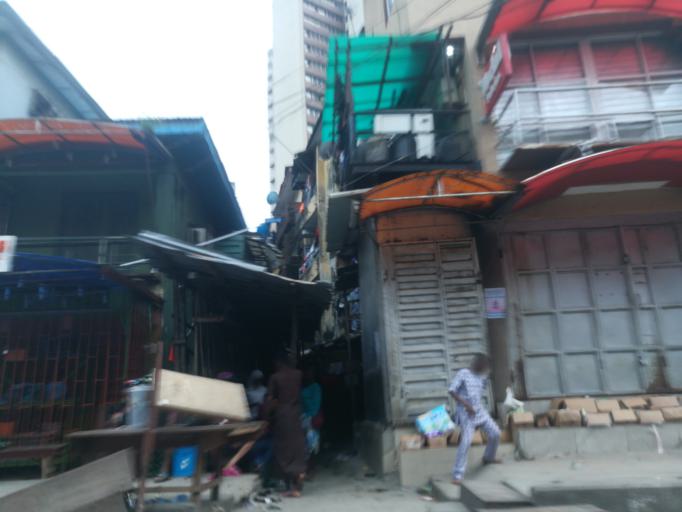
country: NG
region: Lagos
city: Lagos
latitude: 6.4585
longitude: 3.3857
